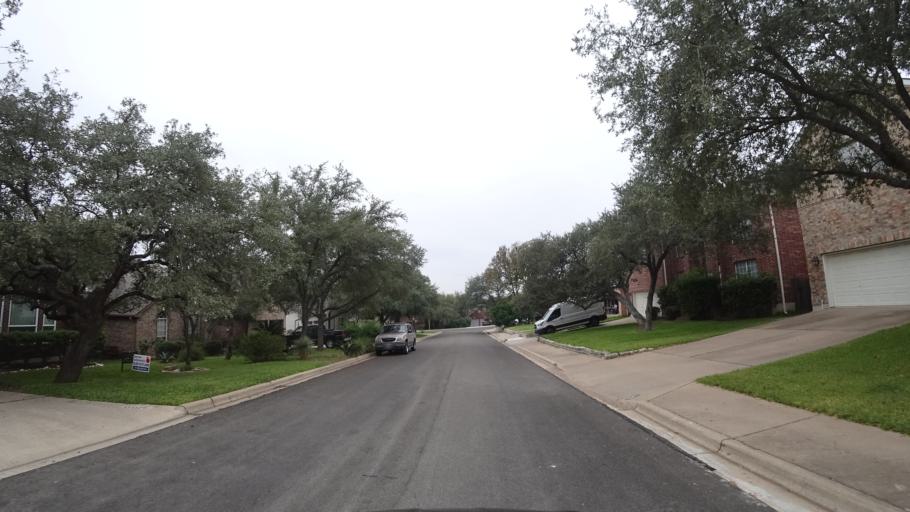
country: US
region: Texas
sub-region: Travis County
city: Shady Hollow
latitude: 30.1821
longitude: -97.8928
